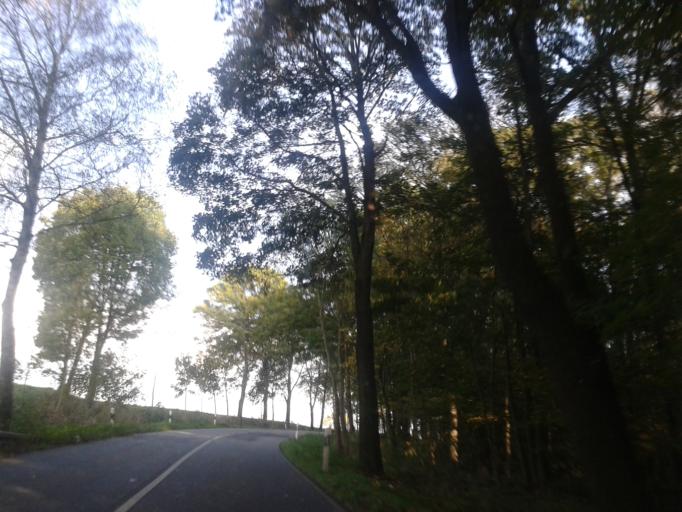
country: DE
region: Saxony
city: Reinsberg
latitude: 51.0535
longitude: 13.3912
